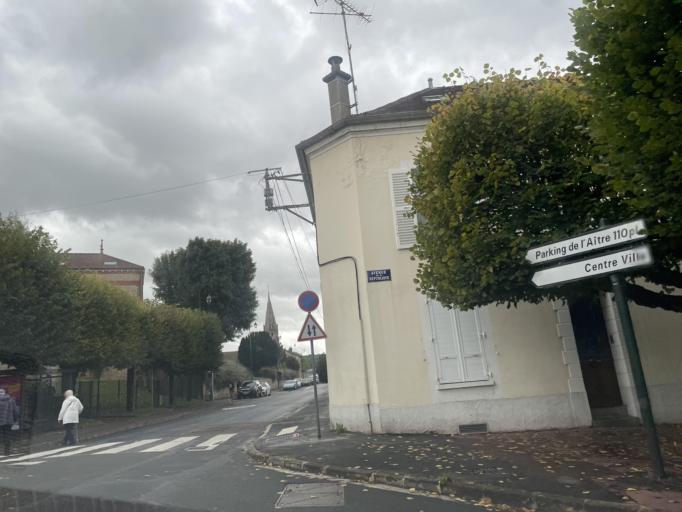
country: FR
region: Ile-de-France
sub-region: Departement de Seine-et-Marne
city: Coulommiers
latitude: 48.8155
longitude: 3.0873
